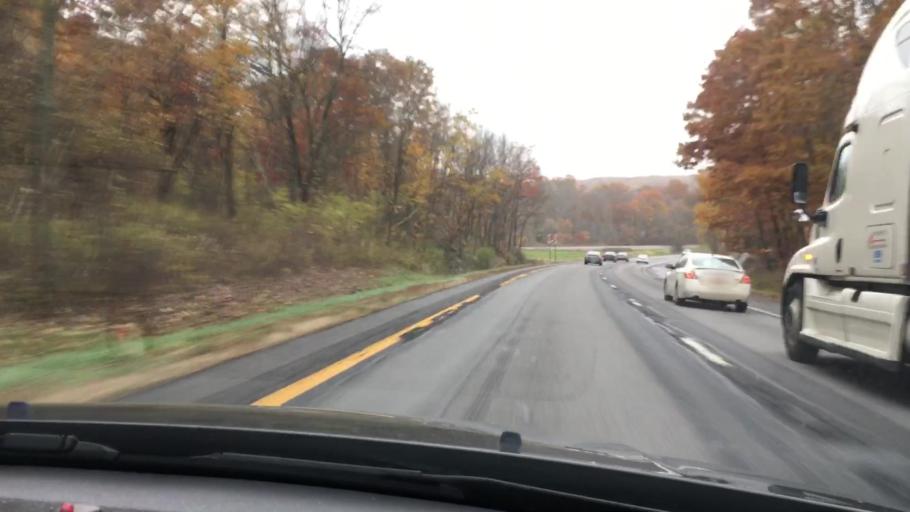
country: US
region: New York
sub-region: Putnam County
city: Lake Carmel
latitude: 41.5018
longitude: -73.6754
